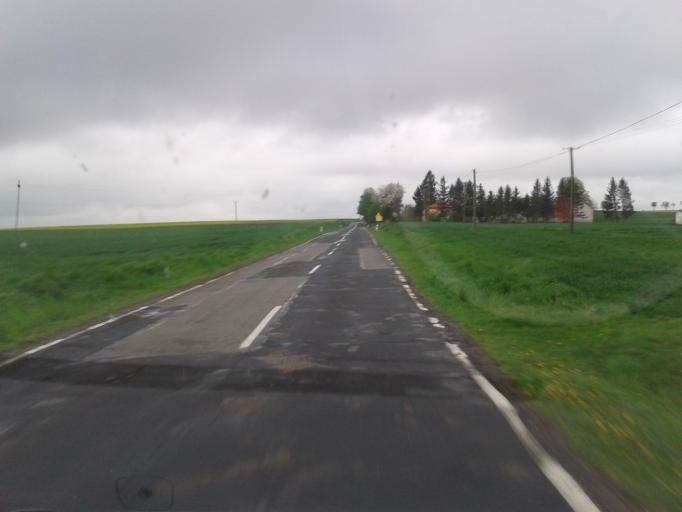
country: PL
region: Lublin Voivodeship
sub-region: Powiat hrubieszowski
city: Dolhobyczow
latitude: 50.5747
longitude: 23.9644
